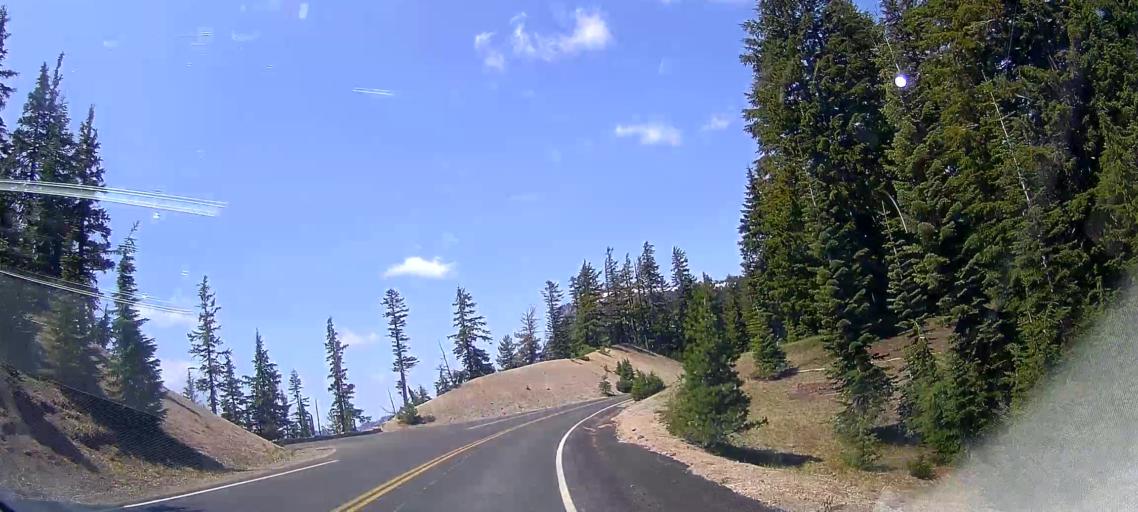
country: US
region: Oregon
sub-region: Jackson County
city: Shady Cove
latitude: 42.9804
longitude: -122.1120
